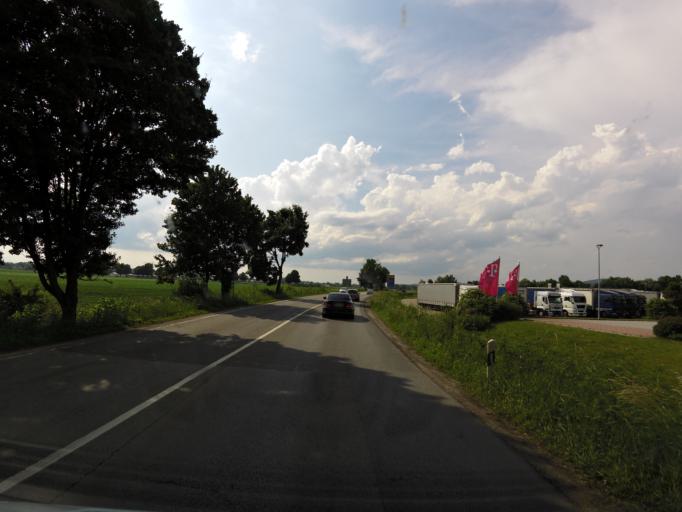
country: DE
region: Bavaria
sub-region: Lower Bavaria
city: Hengersberg
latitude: 48.7663
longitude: 13.0440
